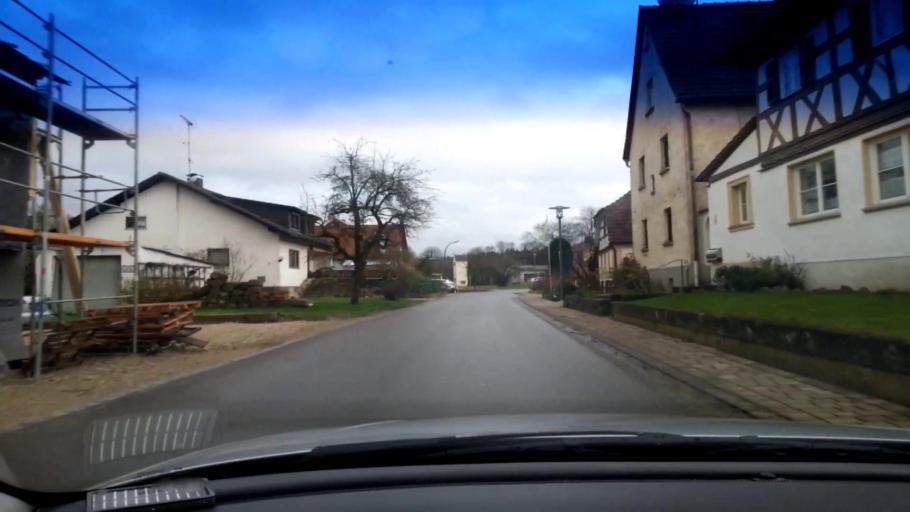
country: DE
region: Bavaria
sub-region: Upper Franconia
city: Ebensfeld
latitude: 50.0316
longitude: 10.9725
